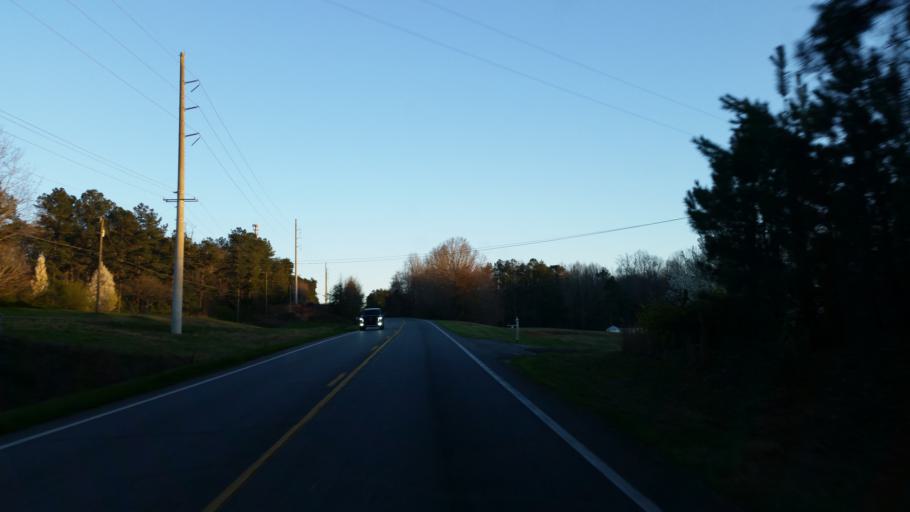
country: US
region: Georgia
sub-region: Dawson County
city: Dawsonville
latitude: 34.3259
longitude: -84.0081
